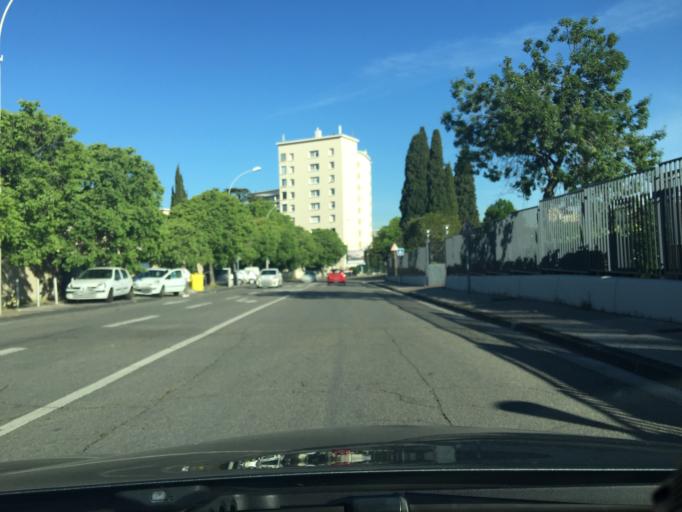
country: FR
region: Provence-Alpes-Cote d'Azur
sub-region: Departement des Bouches-du-Rhone
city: Marseille 09
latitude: 43.2563
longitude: 5.4049
